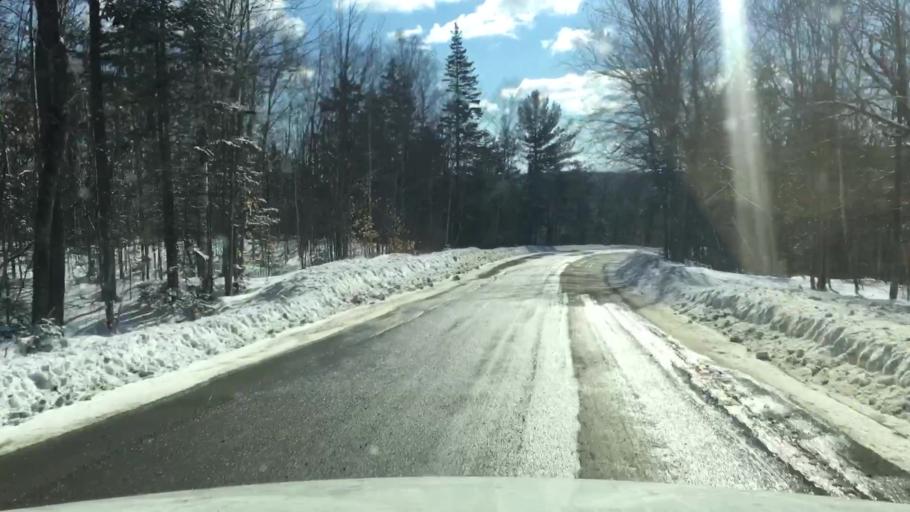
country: US
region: Maine
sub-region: Washington County
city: Calais
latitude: 45.0757
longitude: -67.5024
